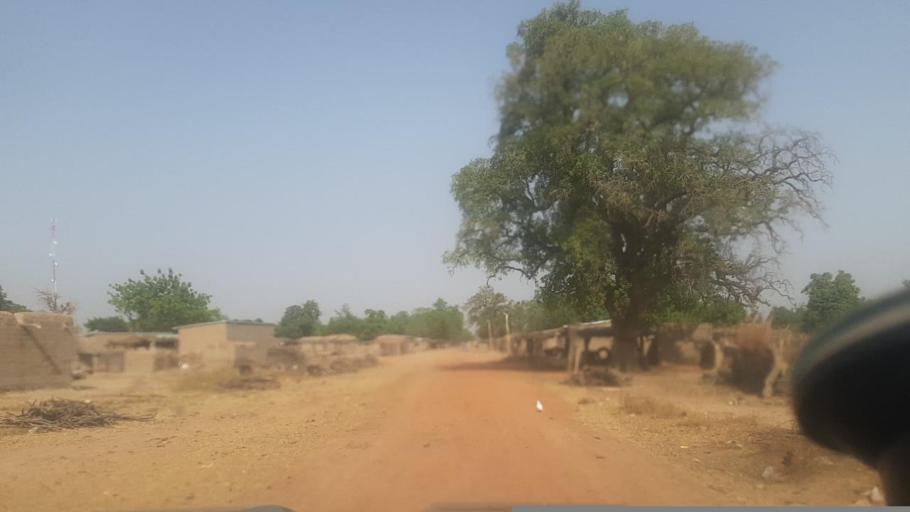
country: ML
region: Segou
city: Bla
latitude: 12.8466
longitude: -5.9927
